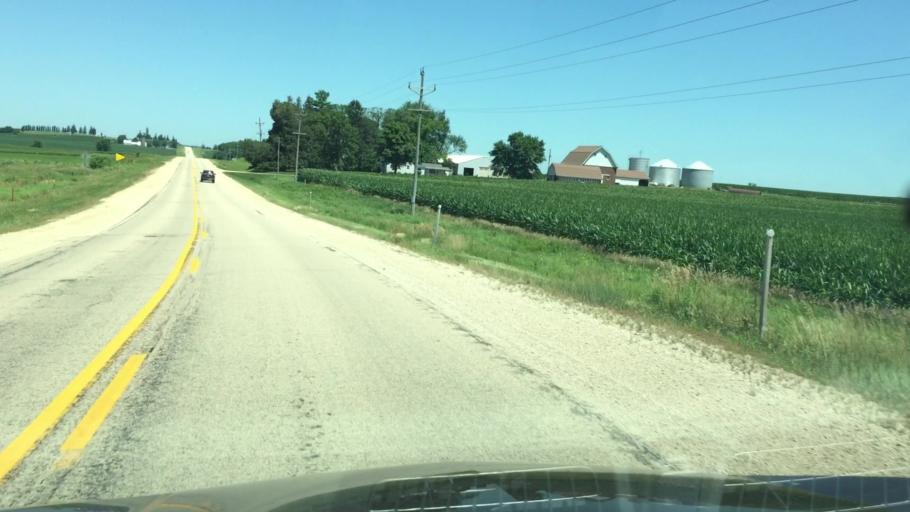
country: US
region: Iowa
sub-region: Cedar County
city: Mechanicsville
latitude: 41.9639
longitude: -91.1421
